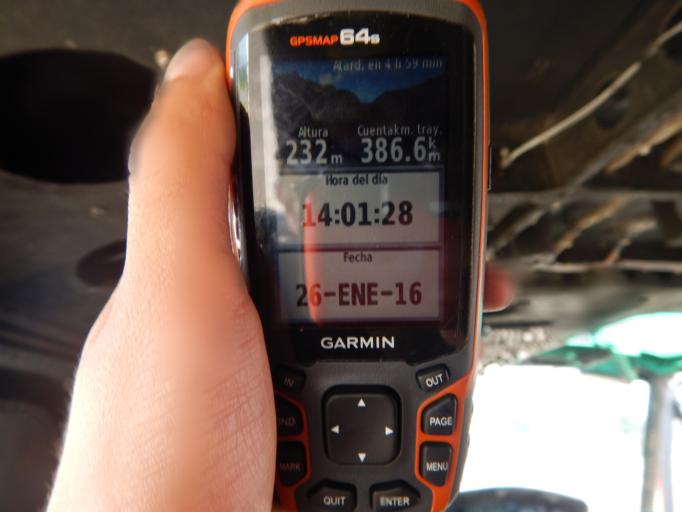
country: BO
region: Cochabamba
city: Chimore
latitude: -16.9928
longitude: -65.1412
